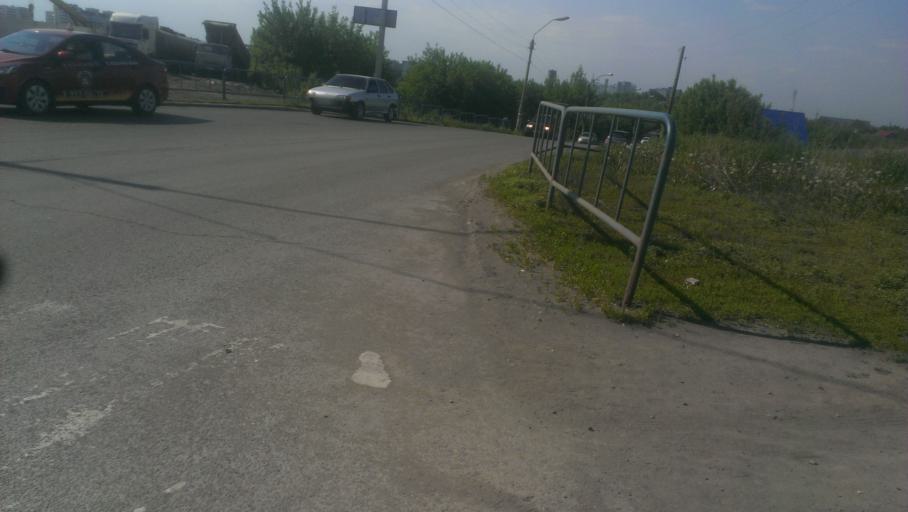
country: RU
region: Altai Krai
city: Novoaltaysk
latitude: 53.4023
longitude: 83.9463
